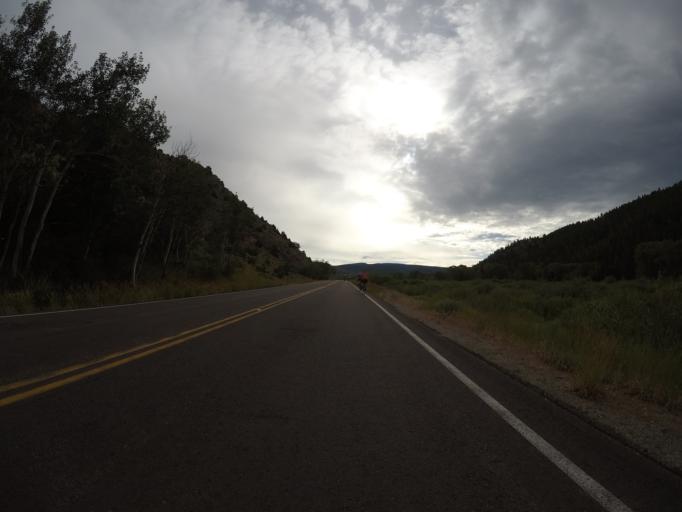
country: US
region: Wyoming
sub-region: Carbon County
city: Saratoga
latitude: 41.3597
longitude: -106.5679
